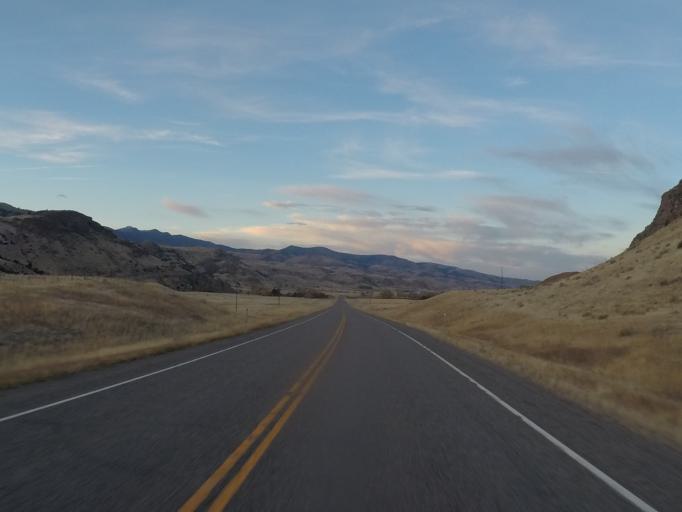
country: US
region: Montana
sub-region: Gallatin County
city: Bozeman
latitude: 45.2414
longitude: -110.8701
